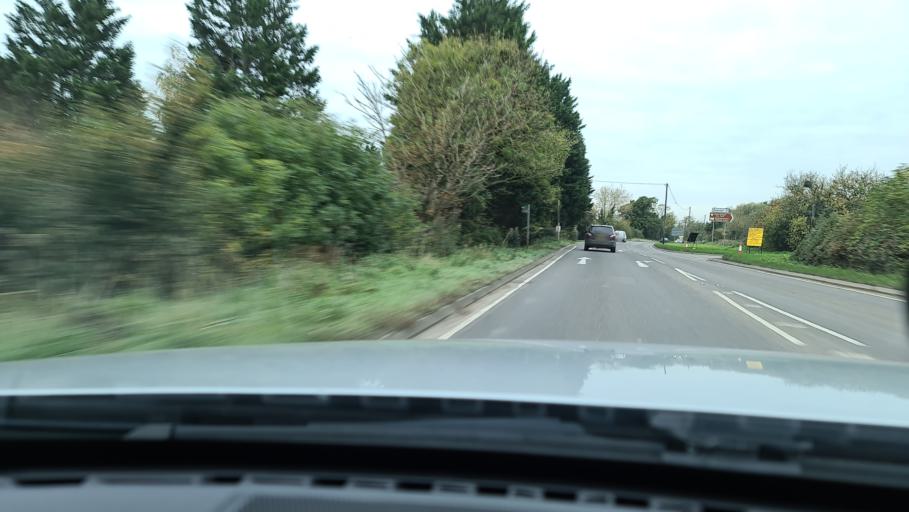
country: GB
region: England
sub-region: Buckinghamshire
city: Waddesdon
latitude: 51.8519
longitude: -0.9460
